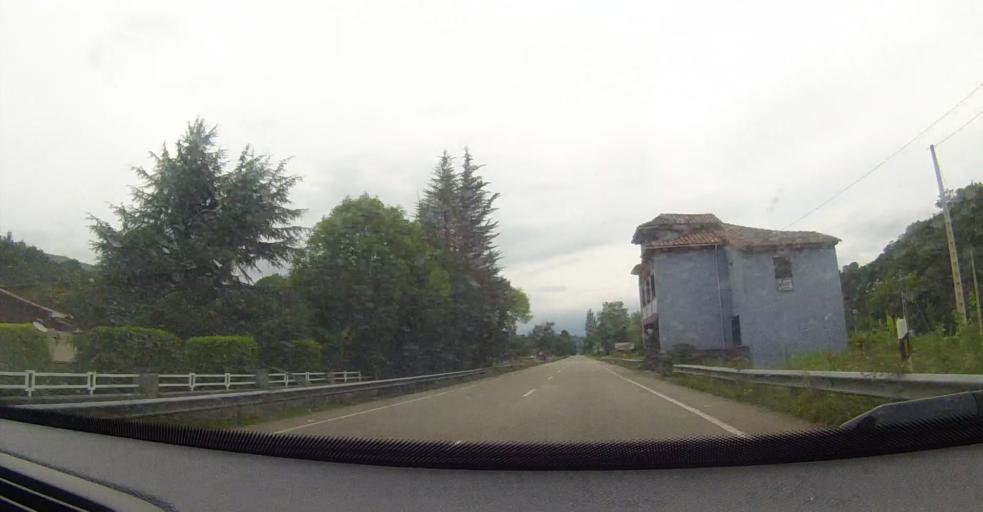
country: ES
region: Asturias
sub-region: Province of Asturias
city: Pilona
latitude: 43.3570
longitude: -5.3115
